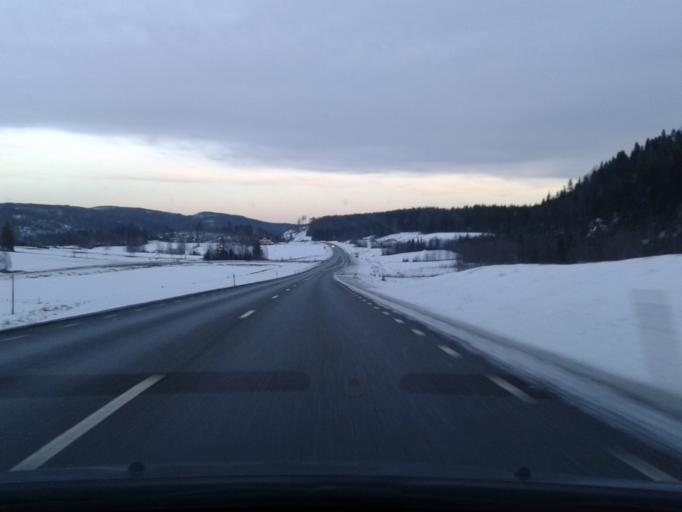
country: SE
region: Vaesternorrland
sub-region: Kramfors Kommun
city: Bollstabruk
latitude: 63.0415
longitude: 17.6427
